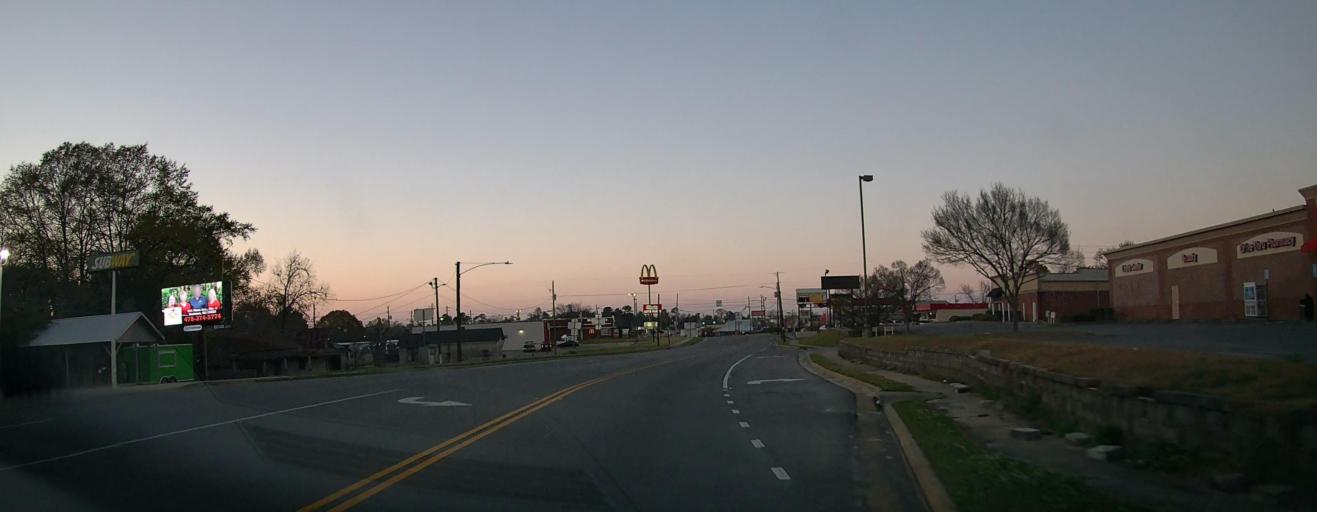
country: US
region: Georgia
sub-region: Dodge County
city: Eastman
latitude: 32.1931
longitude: -83.1755
